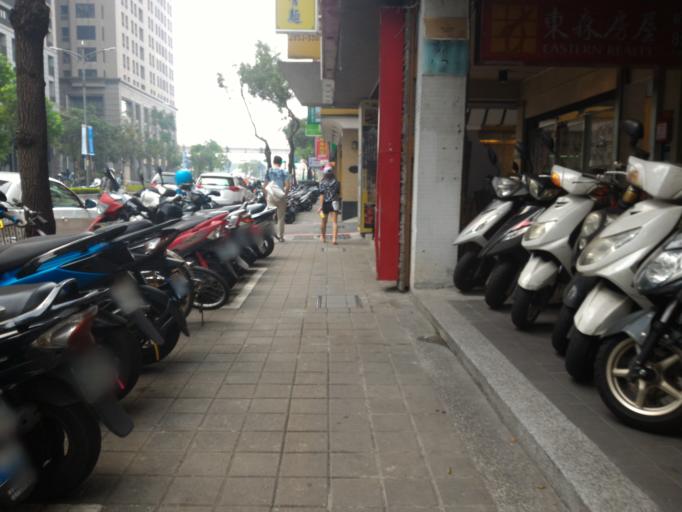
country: TW
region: Taipei
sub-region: Taipei
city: Banqiao
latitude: 25.0146
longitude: 121.4674
